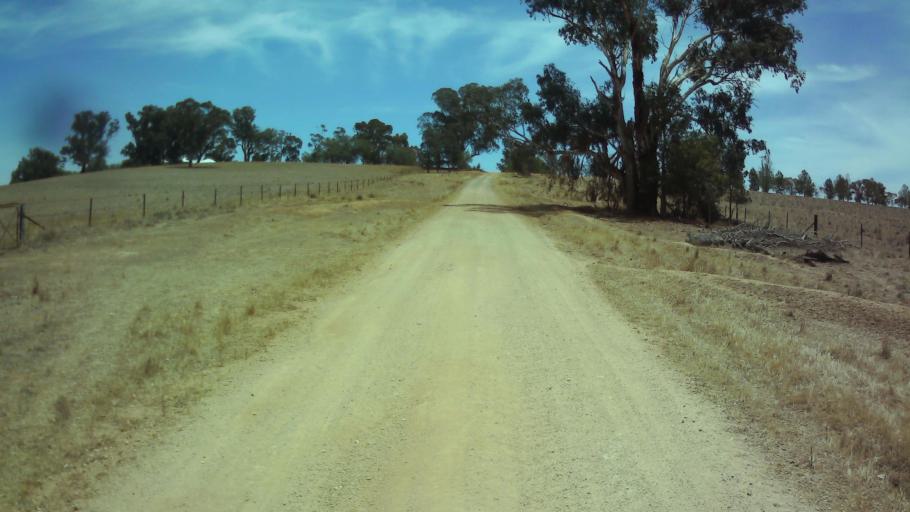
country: AU
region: New South Wales
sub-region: Weddin
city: Grenfell
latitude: -34.0200
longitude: 148.4269
